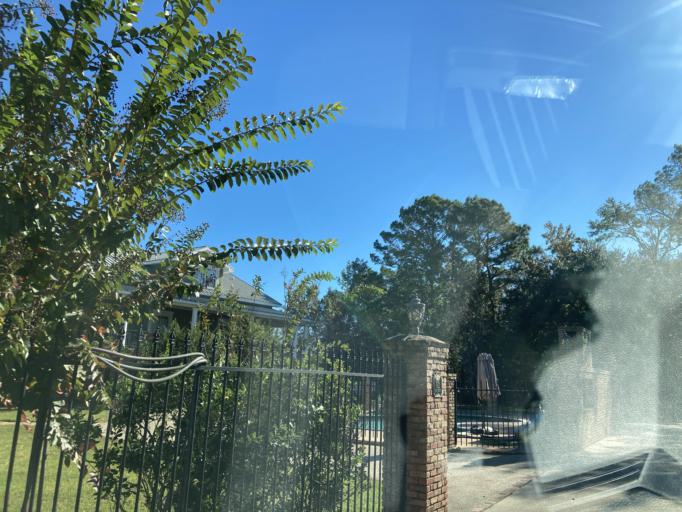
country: US
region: Mississippi
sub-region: Jackson County
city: Gulf Hills
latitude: 30.4226
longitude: -88.8467
